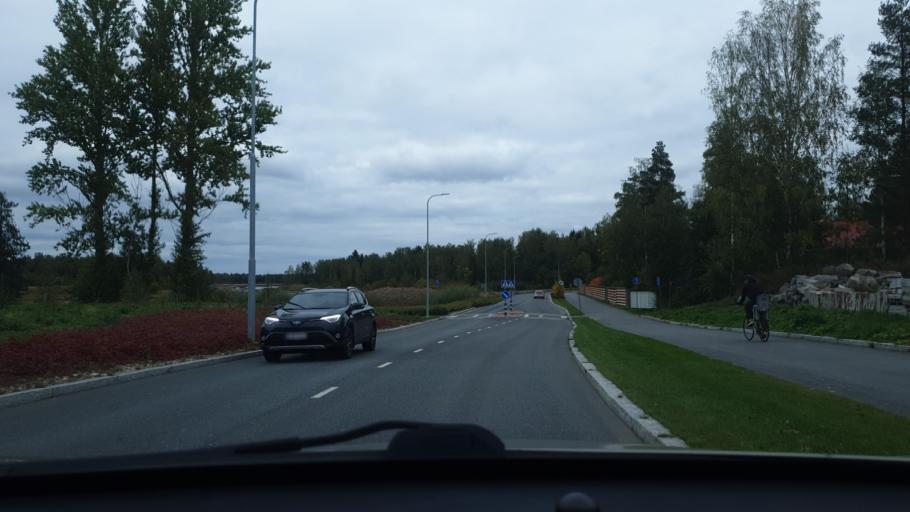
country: FI
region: Ostrobothnia
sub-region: Vaasa
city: Vaasa
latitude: 63.1184
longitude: 21.6204
